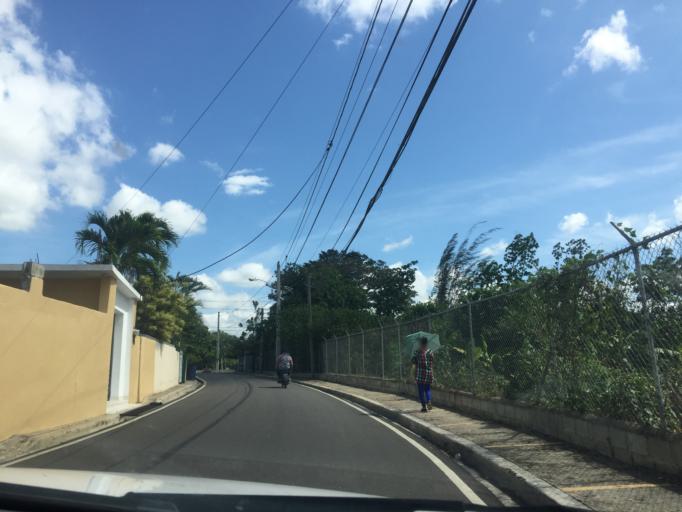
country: DO
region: Santiago
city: Licey al Medio
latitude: 19.3768
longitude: -70.6000
